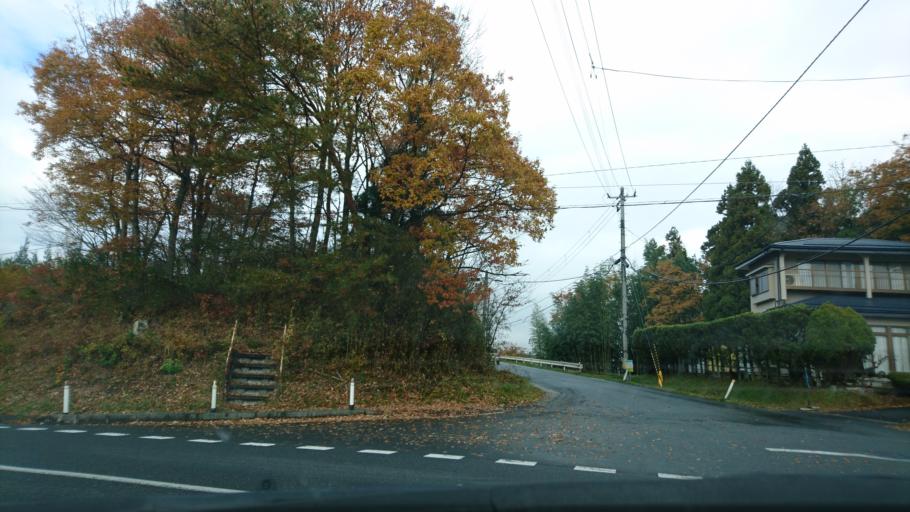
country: JP
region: Iwate
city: Ichinoseki
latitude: 38.8988
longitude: 141.1958
